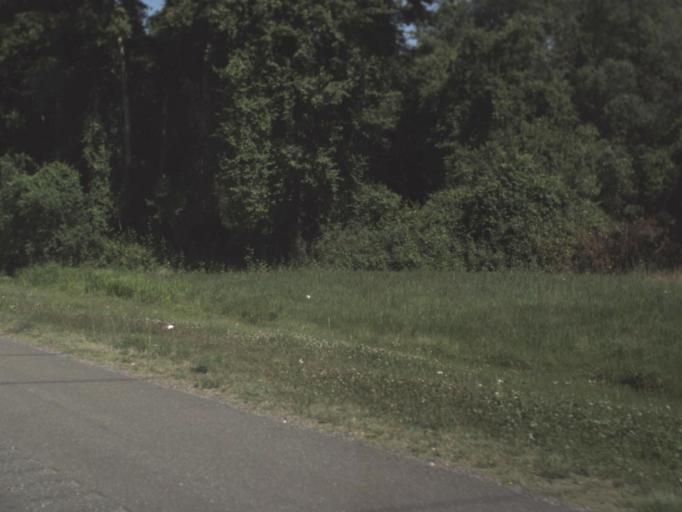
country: US
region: Florida
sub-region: Clay County
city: Bellair-Meadowbrook Terrace
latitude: 30.3120
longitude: -81.8195
